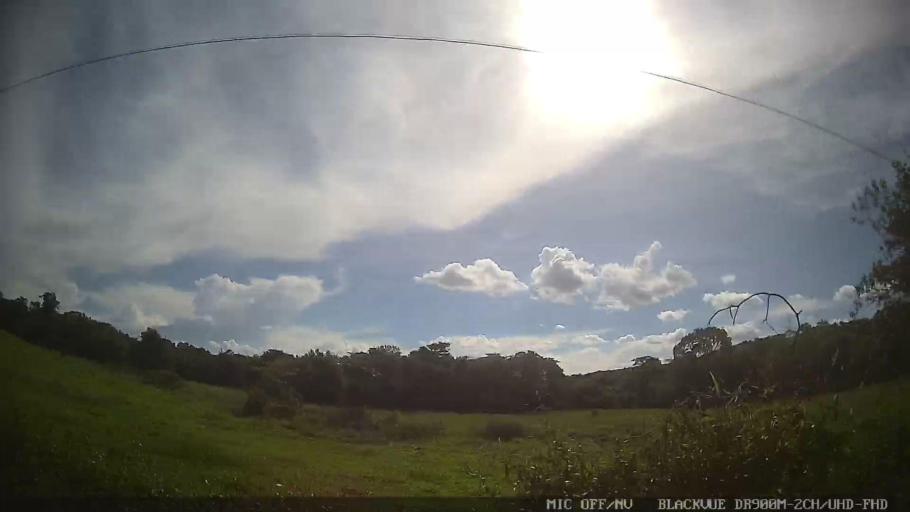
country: BR
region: Sao Paulo
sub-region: Conchas
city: Conchas
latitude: -23.0607
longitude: -47.9791
